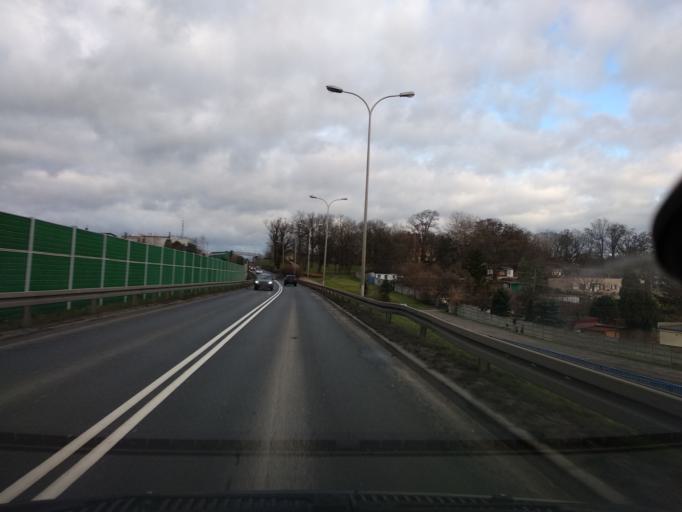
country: PL
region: Greater Poland Voivodeship
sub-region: Kalisz
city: Kalisz
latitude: 51.7737
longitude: 18.0752
